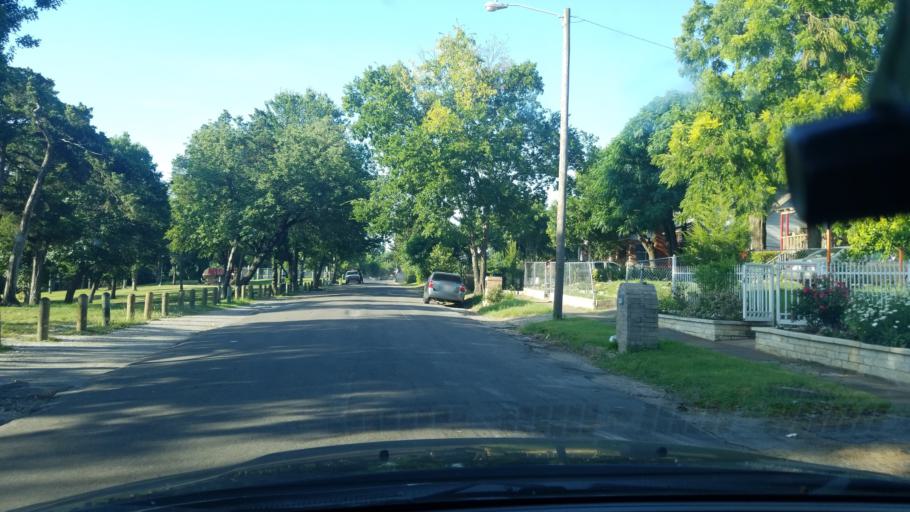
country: US
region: Texas
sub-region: Dallas County
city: Dallas
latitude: 32.7247
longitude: -96.8193
